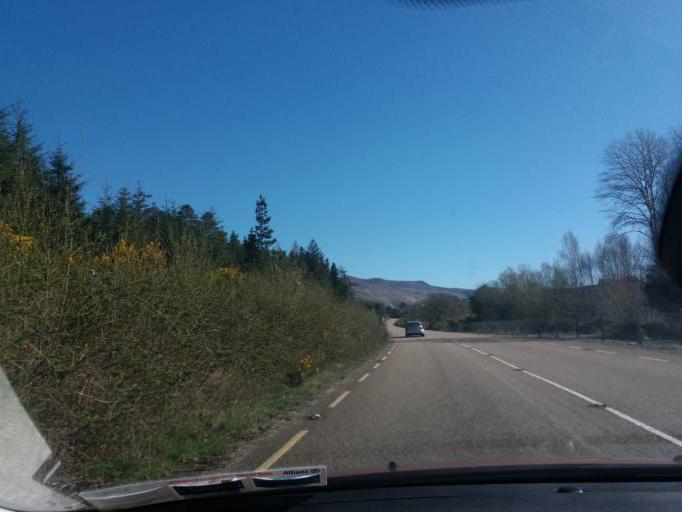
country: IE
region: Munster
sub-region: Ciarrai
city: Cill Airne
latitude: 51.9610
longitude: -9.3655
